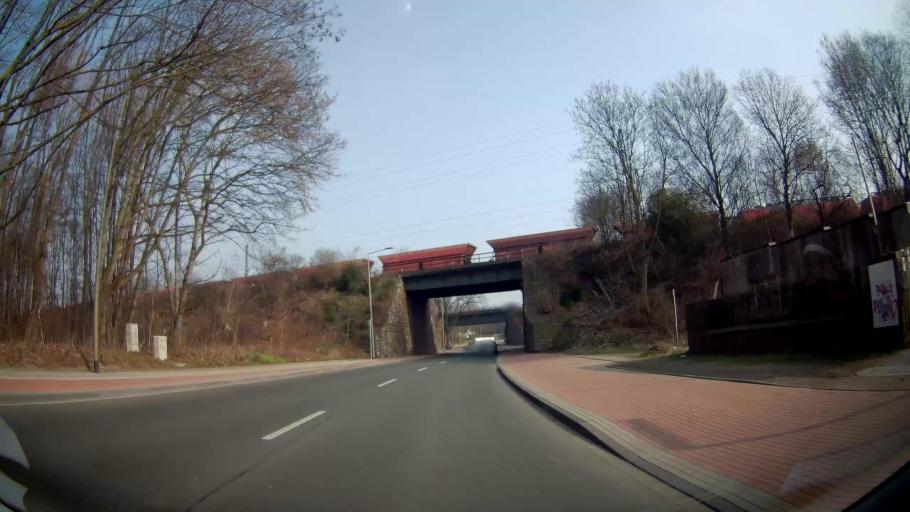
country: DE
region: North Rhine-Westphalia
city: Meiderich
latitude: 51.4604
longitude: 6.8006
